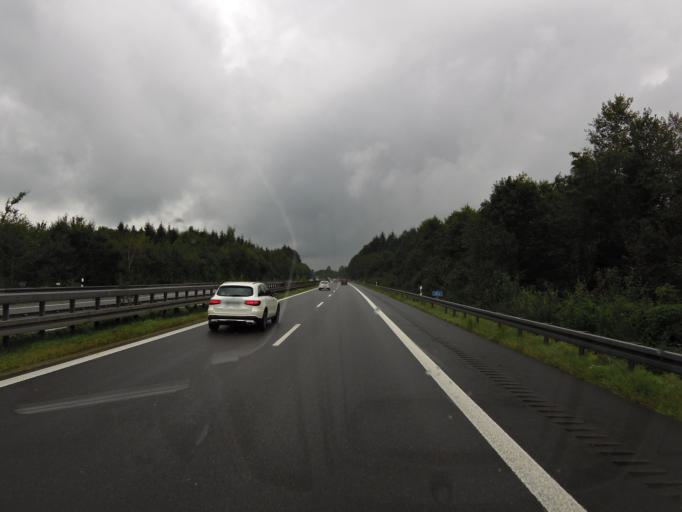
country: DE
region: Bavaria
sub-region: Swabia
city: Hergensweiler
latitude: 47.6521
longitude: 9.7616
